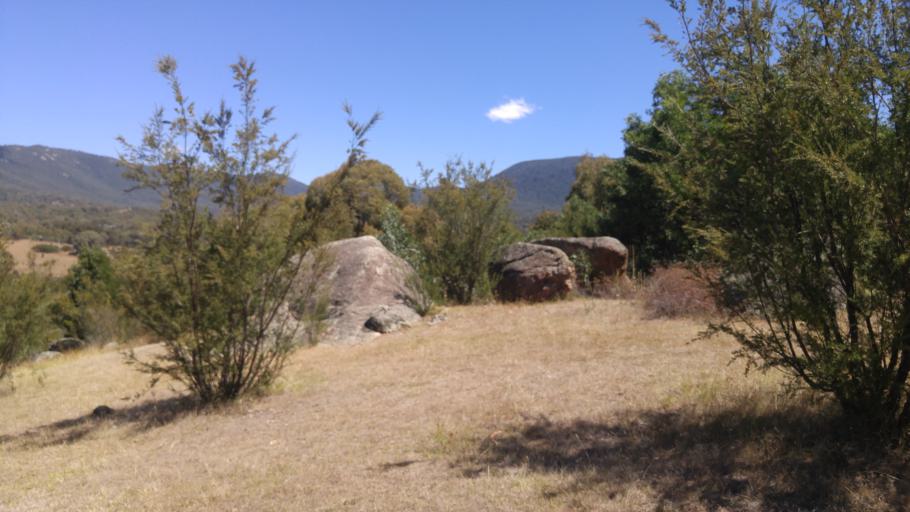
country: AU
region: Australian Capital Territory
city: Macarthur
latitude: -35.4497
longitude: 148.9251
